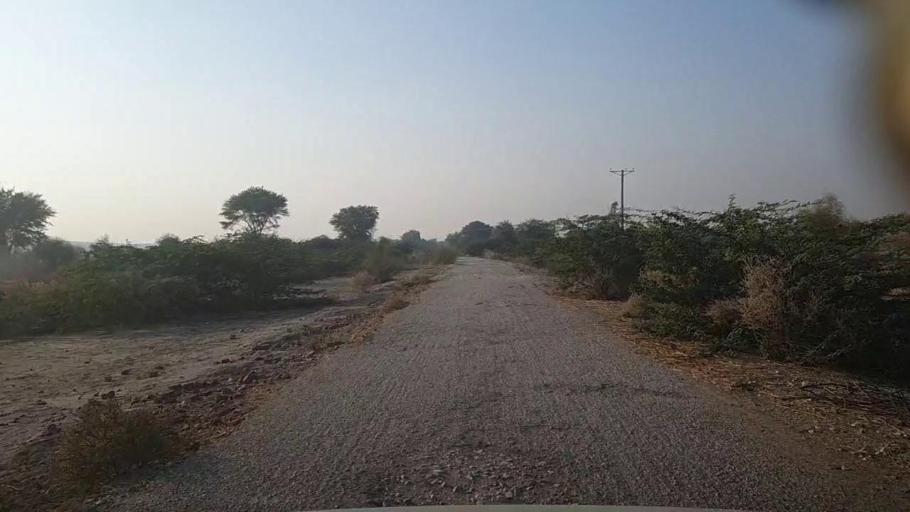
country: PK
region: Sindh
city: Pad Idan
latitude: 26.7212
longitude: 68.4536
